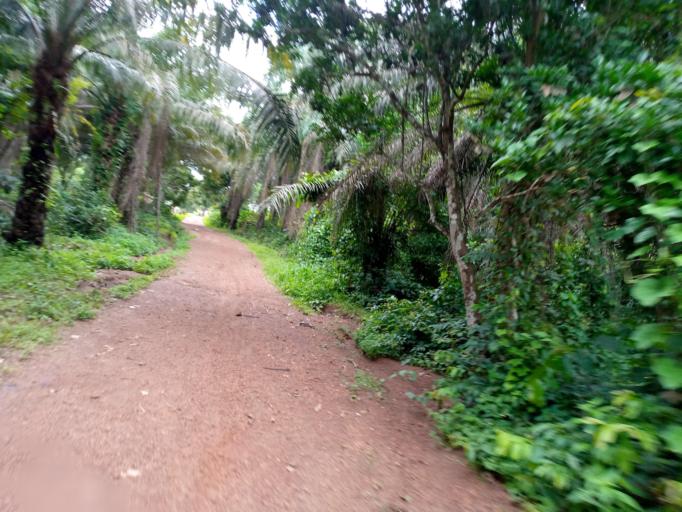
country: SL
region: Northern Province
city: Mange
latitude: 8.9732
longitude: -12.8306
